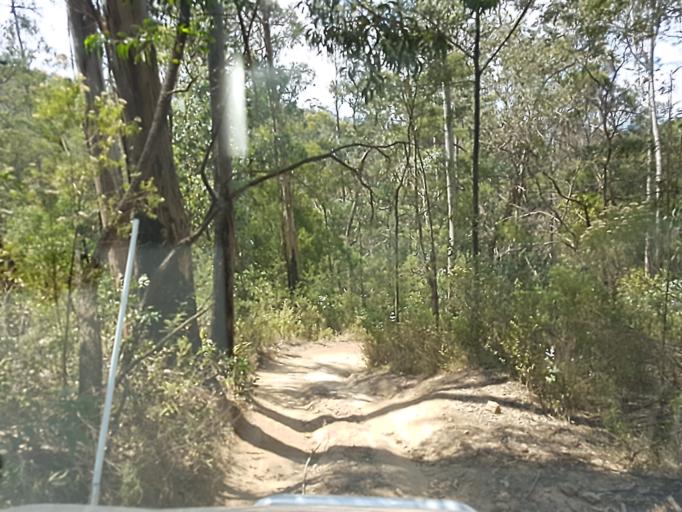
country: AU
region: Victoria
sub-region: East Gippsland
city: Lakes Entrance
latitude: -37.4018
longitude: 148.3176
